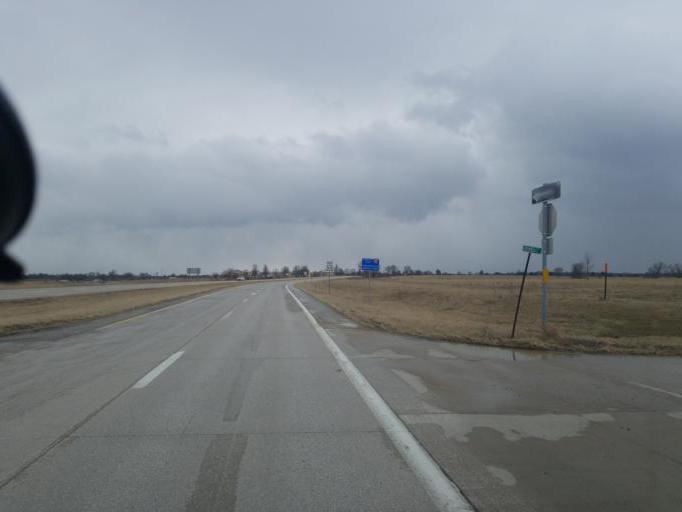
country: US
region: Missouri
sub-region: Macon County
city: Macon
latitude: 39.8024
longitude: -92.4746
